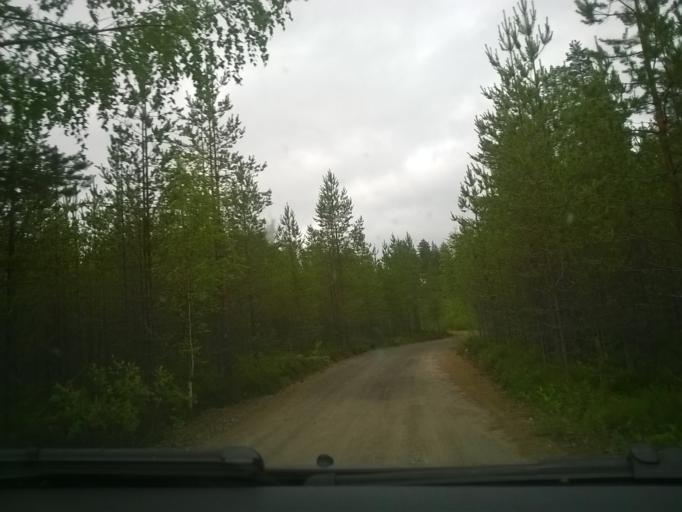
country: FI
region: Kainuu
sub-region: Kehys-Kainuu
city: Kuhmo
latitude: 64.1477
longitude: 29.4095
